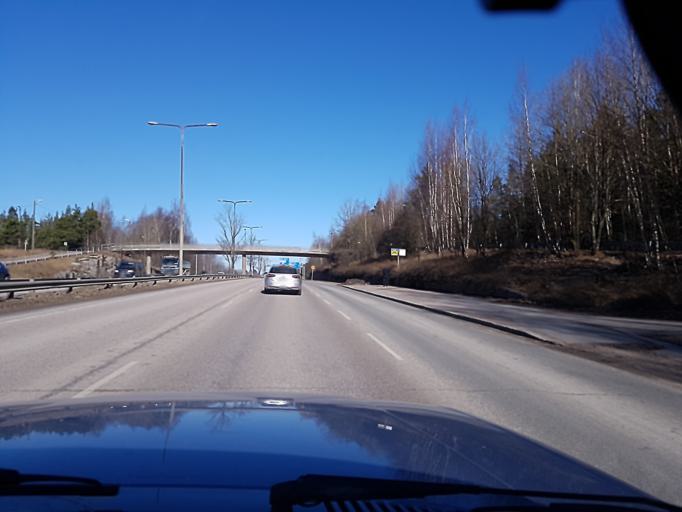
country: FI
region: Uusimaa
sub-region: Helsinki
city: Helsinki
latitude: 60.2321
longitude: 24.9031
